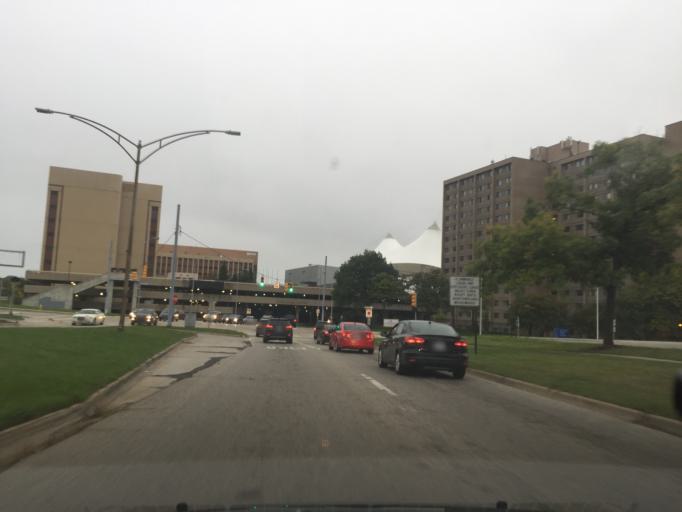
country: US
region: Michigan
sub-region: Oakland County
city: Pontiac
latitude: 42.6343
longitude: -83.2875
